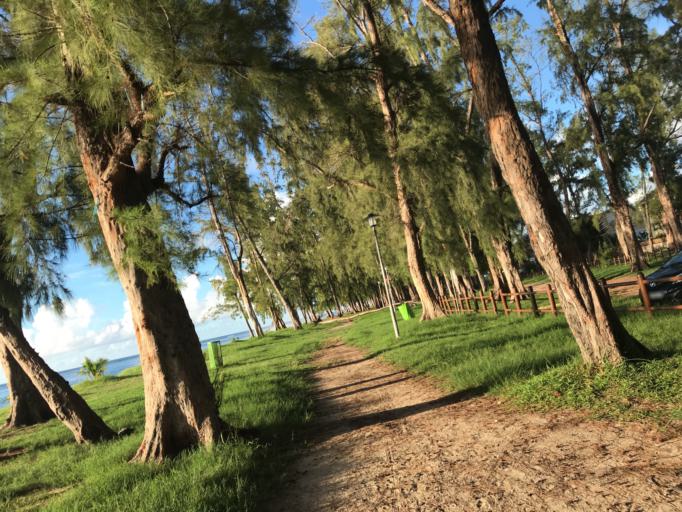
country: MU
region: Black River
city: Flic en Flac
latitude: -20.2895
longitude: 57.3634
